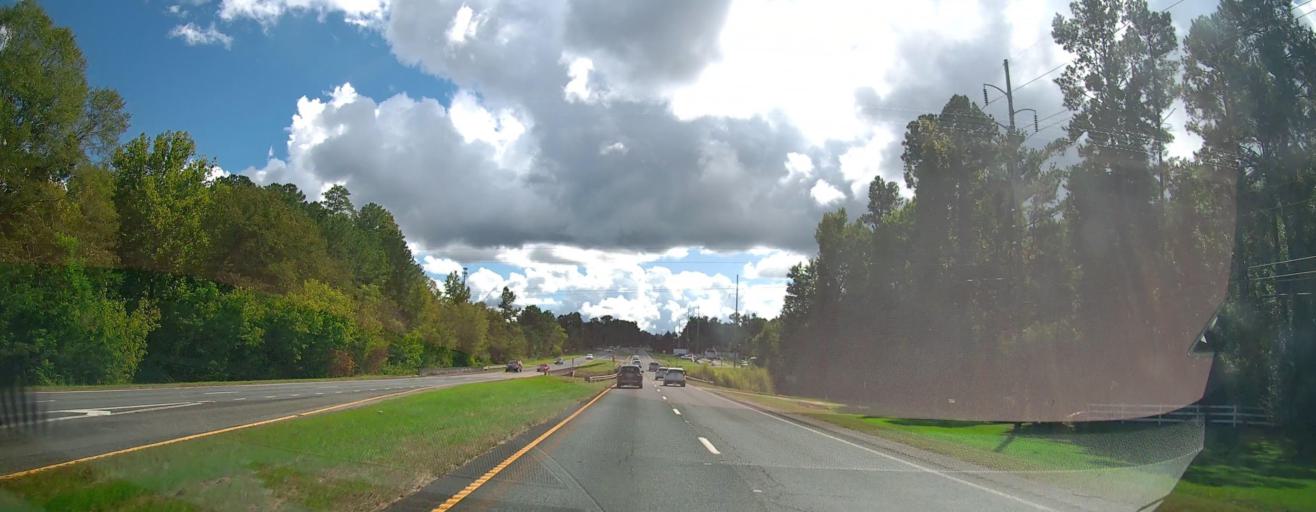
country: US
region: Georgia
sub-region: Jones County
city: Gray
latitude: 32.9498
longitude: -83.5798
